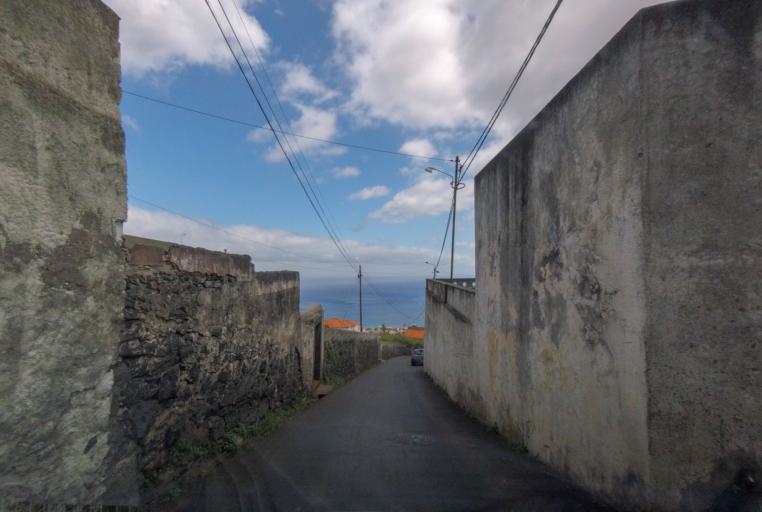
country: PT
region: Madeira
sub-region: Funchal
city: Nossa Senhora do Monte
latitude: 32.6668
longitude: -16.9041
